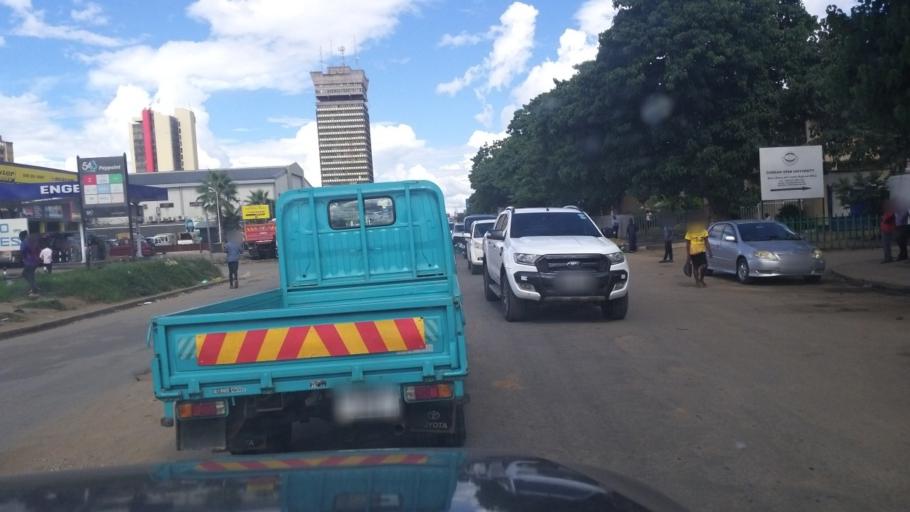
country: ZM
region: Lusaka
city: Lusaka
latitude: -15.4254
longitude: 28.2802
